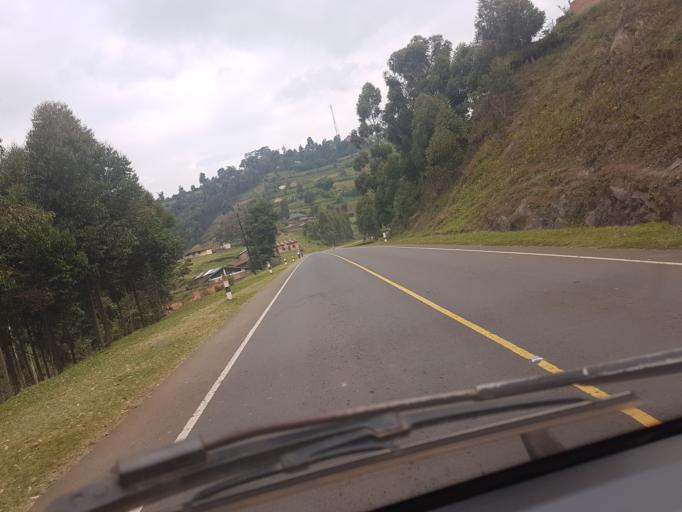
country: UG
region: Western Region
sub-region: Kisoro District
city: Kisoro
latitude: -1.2034
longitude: 29.8119
